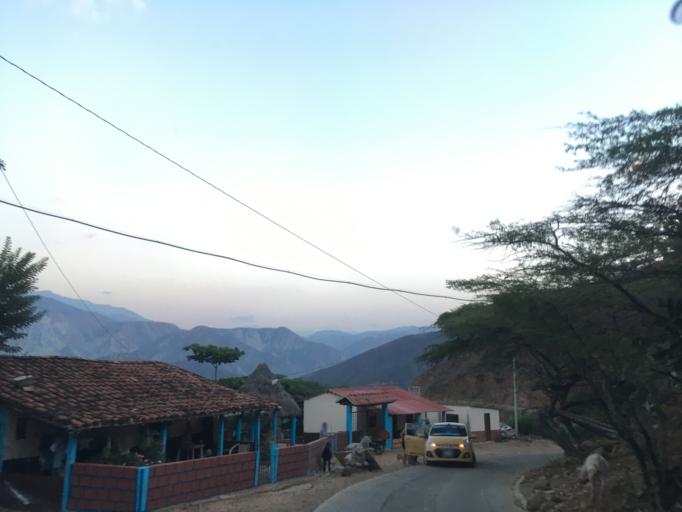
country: CO
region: Santander
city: Aratoca
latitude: 6.7903
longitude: -72.9965
